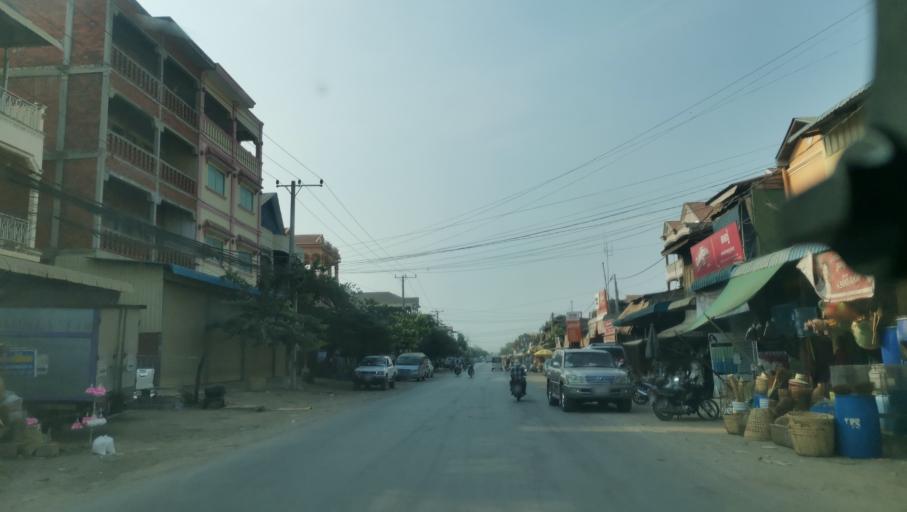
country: KH
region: Battambang
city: Battambang
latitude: 13.1040
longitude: 103.1926
